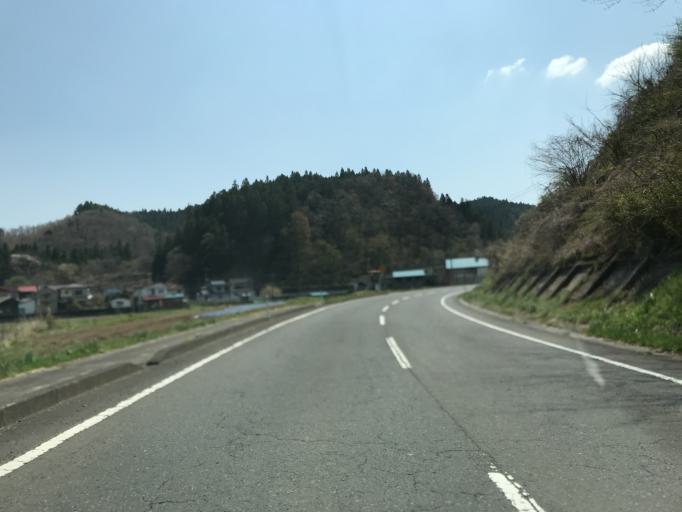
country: JP
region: Fukushima
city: Ishikawa
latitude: 37.0385
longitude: 140.5091
